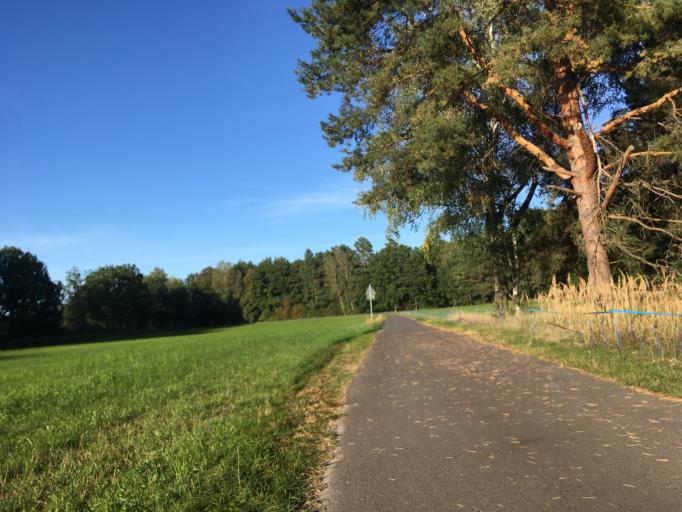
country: PL
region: Lubusz
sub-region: Powiat zarski
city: Trzebiel
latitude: 51.6076
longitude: 14.7614
